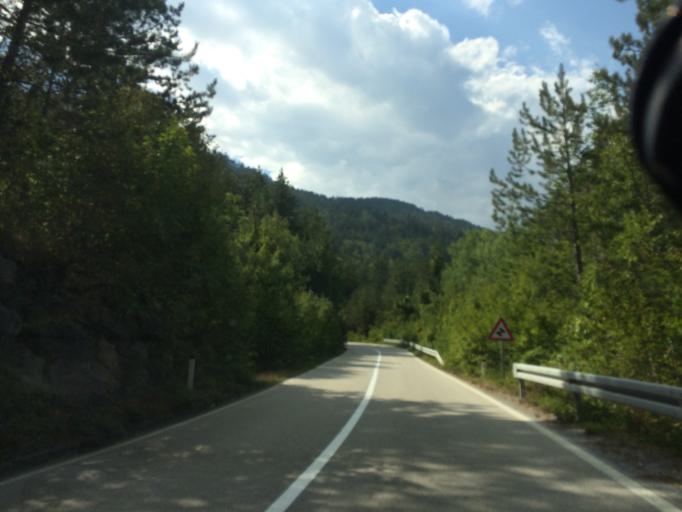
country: ME
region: Opstina Zabljak
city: Zabljak
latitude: 43.1583
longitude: 19.2669
